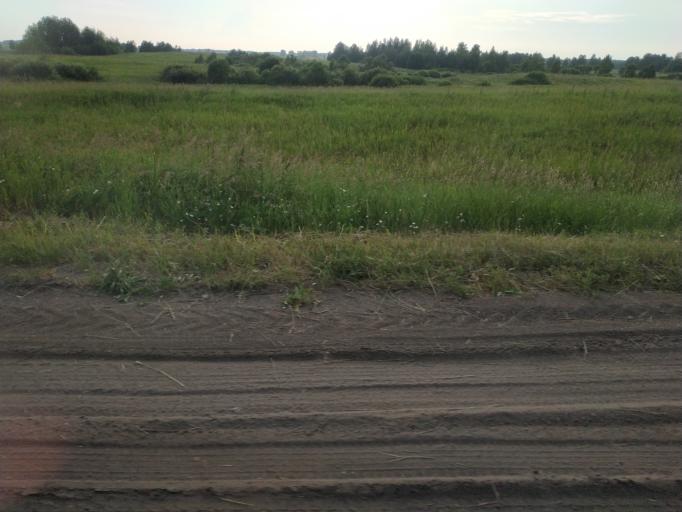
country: RU
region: Sverdlovsk
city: Kamyshlov
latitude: 56.8778
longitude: 62.7122
